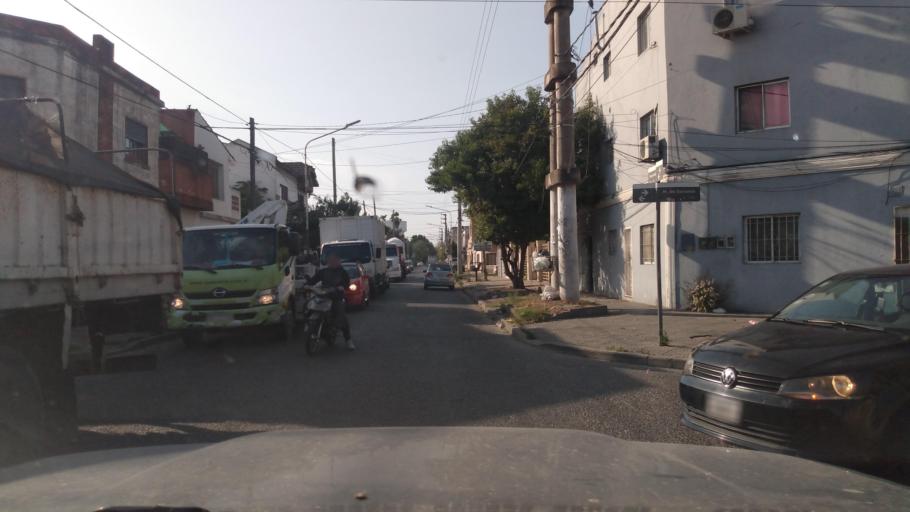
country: AR
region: Buenos Aires
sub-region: Partido de Moron
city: Moron
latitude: -34.6492
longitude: -58.6064
